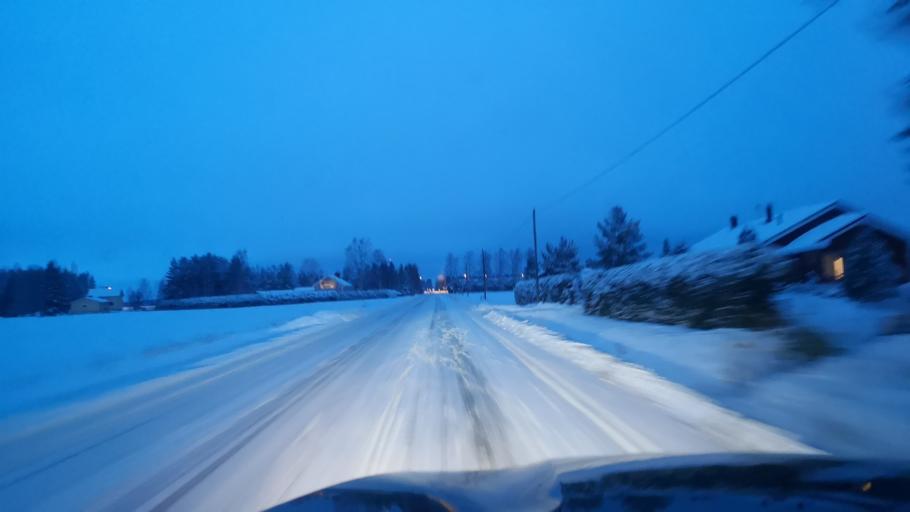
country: FI
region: Varsinais-Suomi
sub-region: Loimaa
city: Loimaa
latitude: 60.8804
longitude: 23.0893
